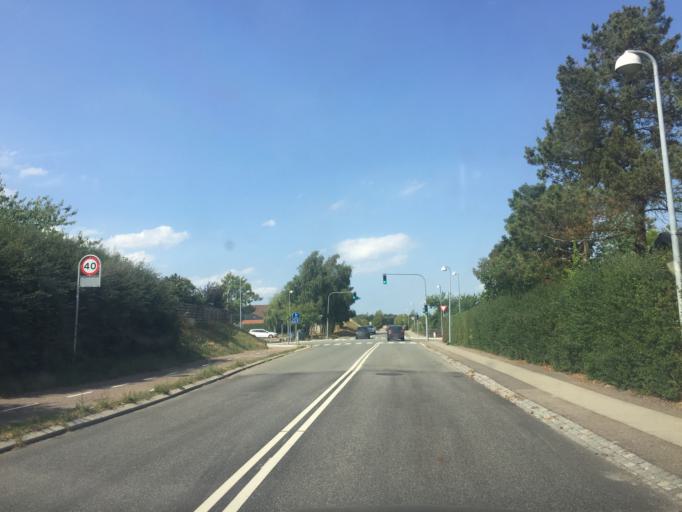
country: DK
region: Zealand
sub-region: Roskilde Kommune
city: Gundsomagle
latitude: 55.7387
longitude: 12.1487
